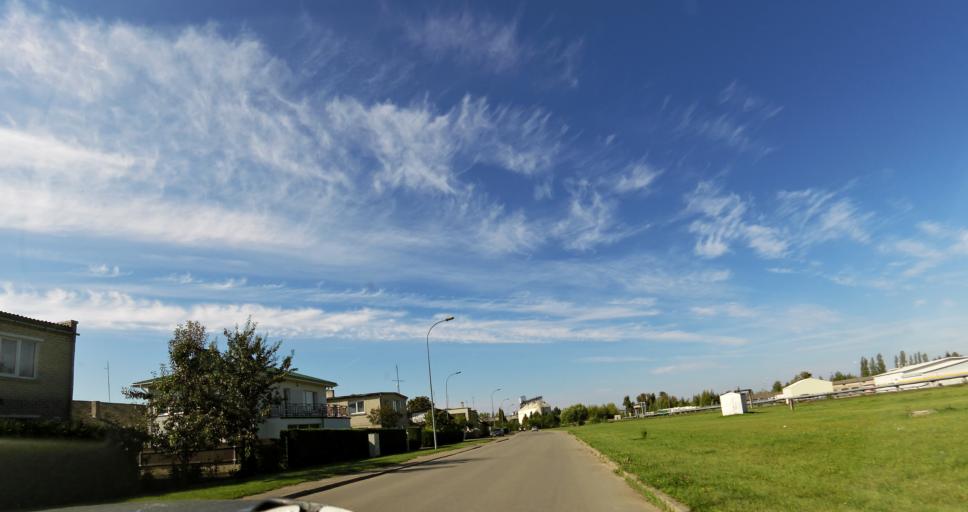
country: LT
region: Panevezys
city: Pasvalys
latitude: 56.0675
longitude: 24.4034
